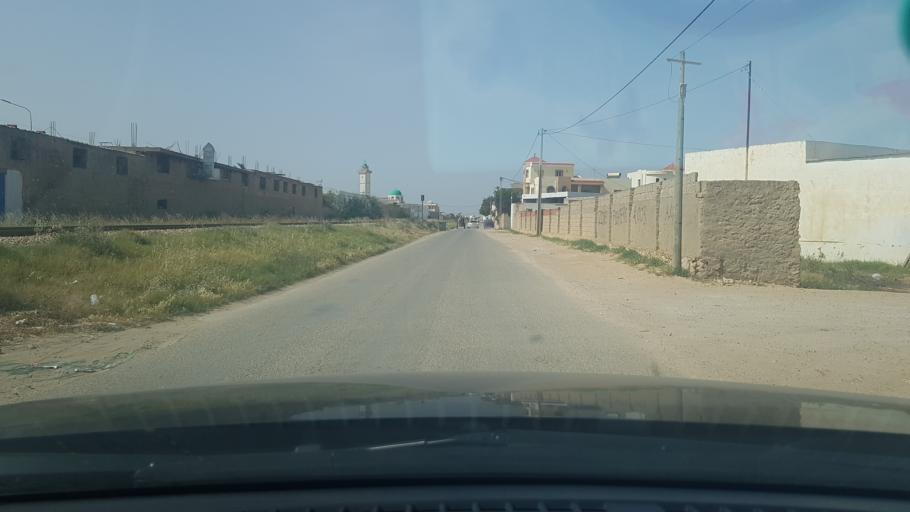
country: TN
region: Safaqis
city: Al Qarmadah
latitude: 34.8195
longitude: 10.7628
